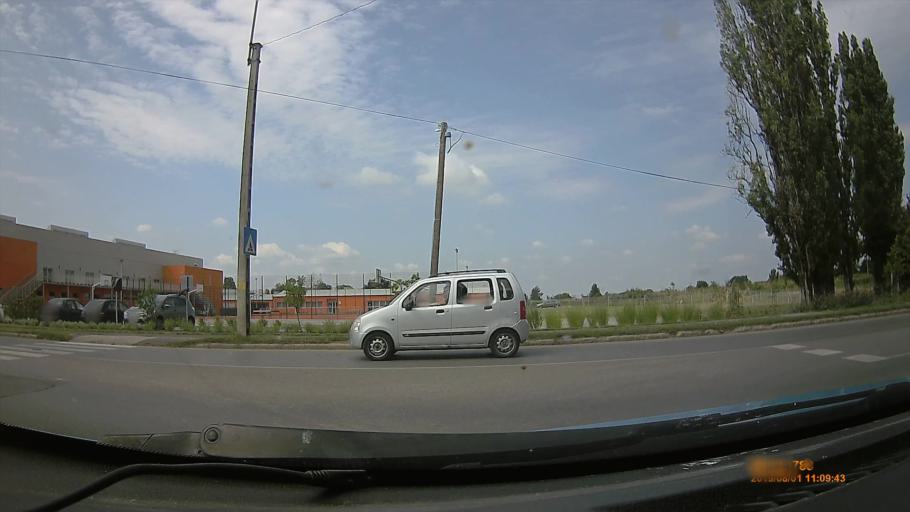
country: HU
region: Baranya
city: Pecs
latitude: 46.0539
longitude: 18.2121
